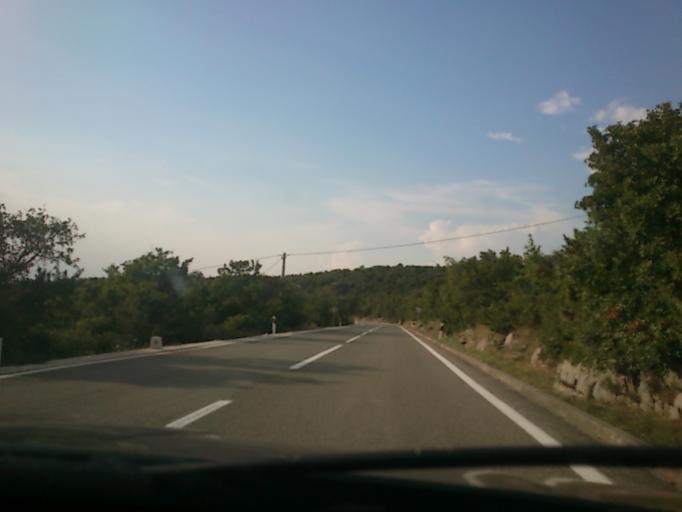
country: HR
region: Primorsko-Goranska
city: Banjol
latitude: 44.7597
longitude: 14.9036
